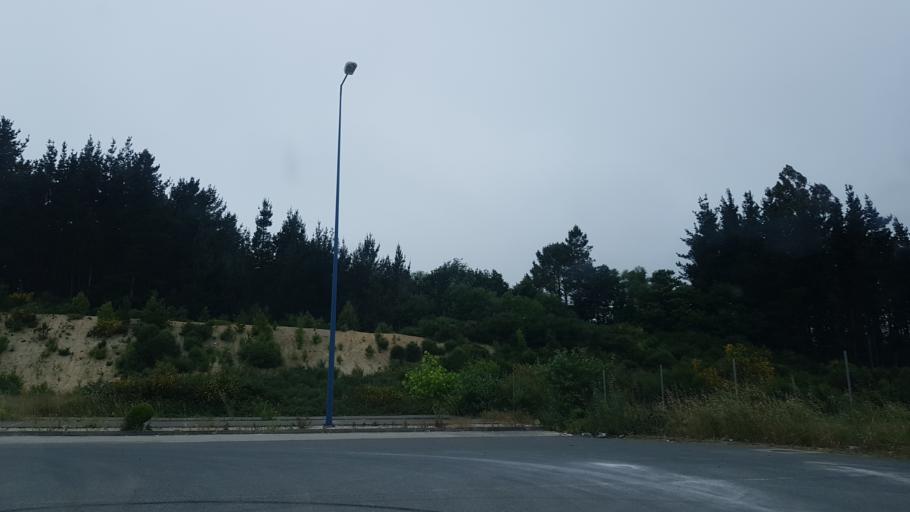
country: ES
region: Galicia
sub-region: Provincia de Lugo
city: Lugo
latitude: 43.0470
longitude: -7.5519
